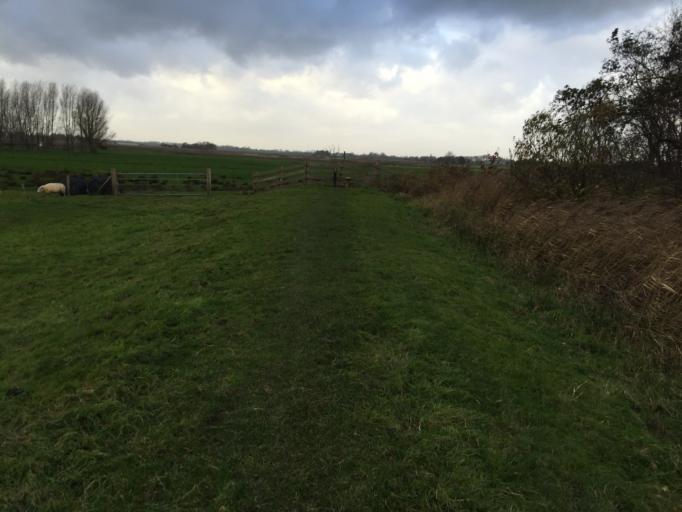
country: NL
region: North Holland
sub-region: Gemeente Ouder-Amstel
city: Ouderkerk aan de Amstel
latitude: 52.2451
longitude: 4.9218
